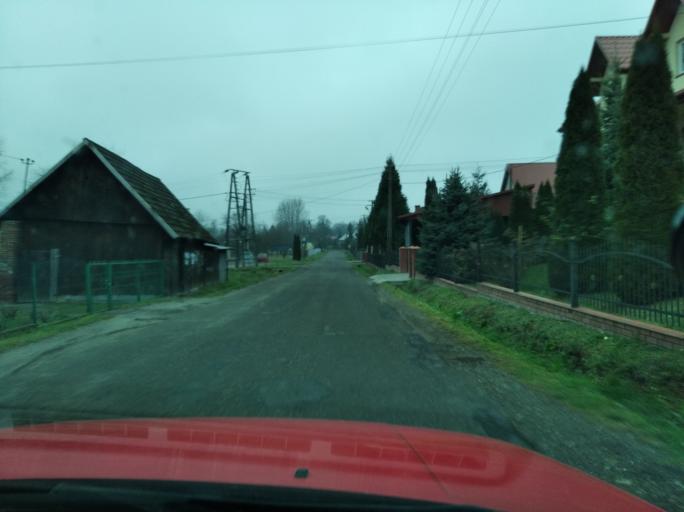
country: PL
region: Subcarpathian Voivodeship
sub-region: Powiat przeworski
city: Mirocin
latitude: 50.0423
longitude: 22.5559
